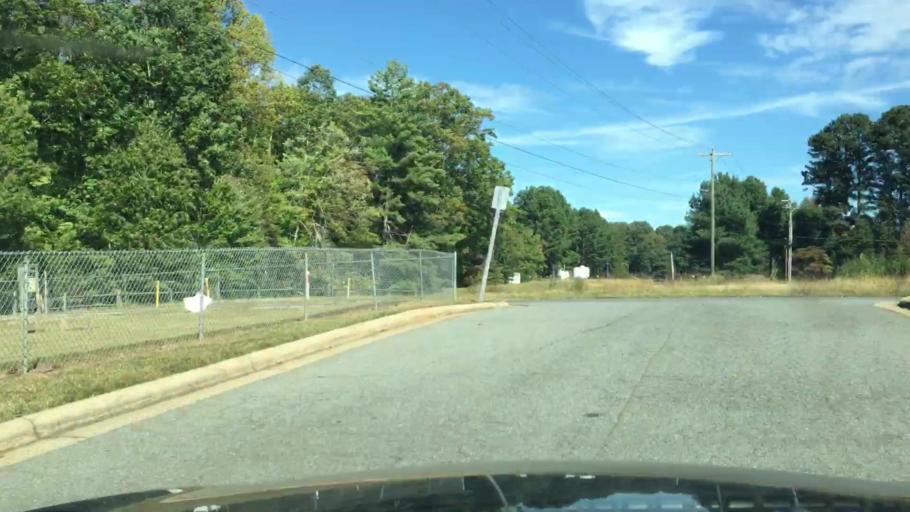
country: US
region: North Carolina
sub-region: Iredell County
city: Mooresville
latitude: 35.5633
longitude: -80.8029
